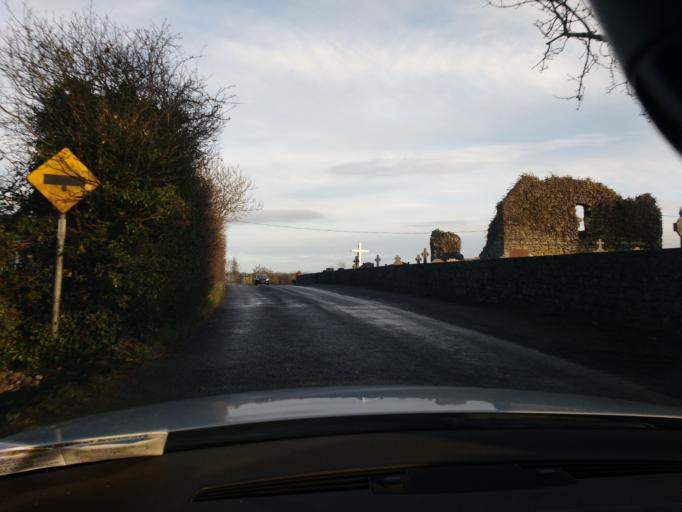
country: IE
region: Munster
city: Thurles
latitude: 52.6328
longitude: -7.7514
